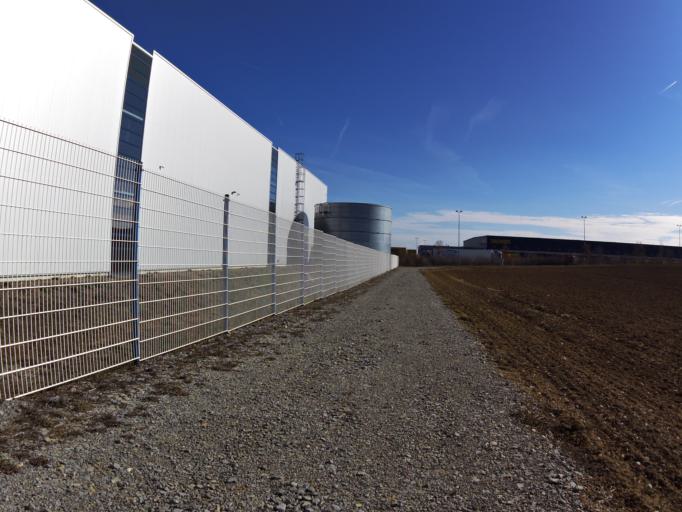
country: DE
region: Bavaria
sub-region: Regierungsbezirk Unterfranken
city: Kurnach
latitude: 49.8526
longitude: 10.0238
